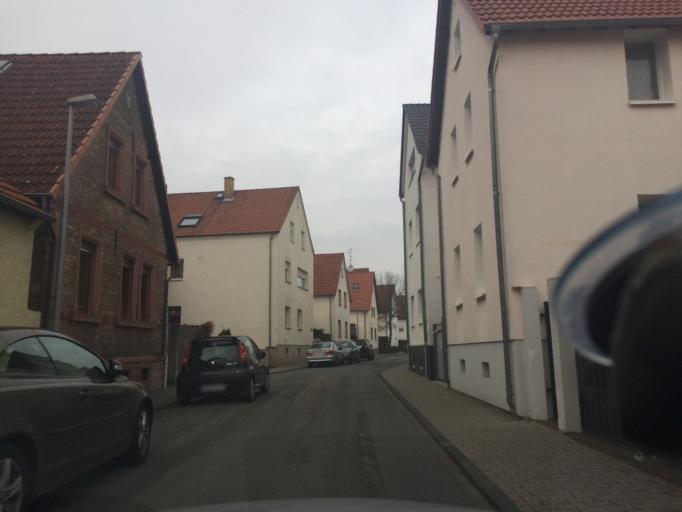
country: DE
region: Hesse
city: Morfelden-Walldorf
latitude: 49.9771
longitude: 8.5727
